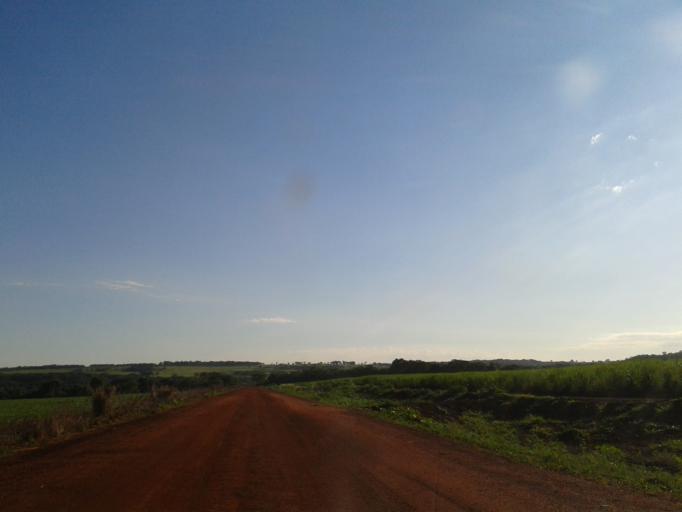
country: BR
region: Minas Gerais
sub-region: Centralina
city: Centralina
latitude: -18.7024
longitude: -49.2830
